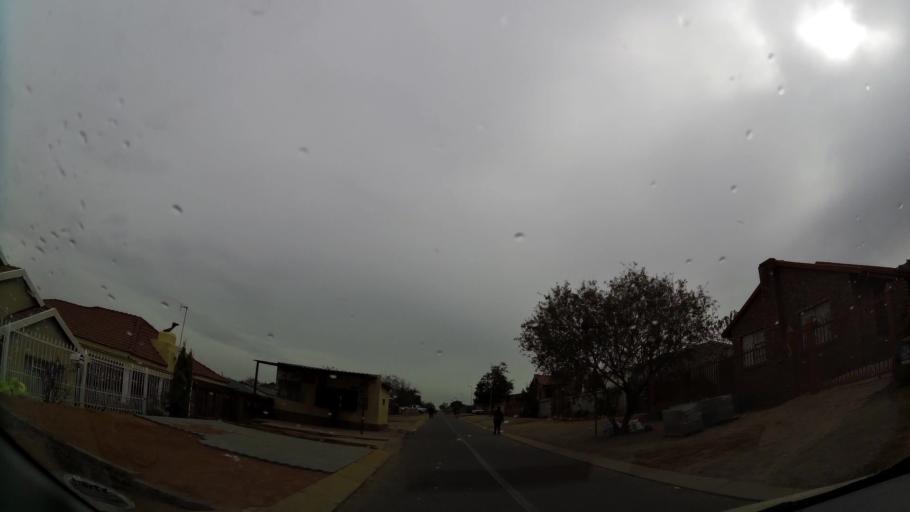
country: ZA
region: Gauteng
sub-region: City of Tshwane Metropolitan Municipality
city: Pretoria
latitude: -25.7022
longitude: 28.3495
